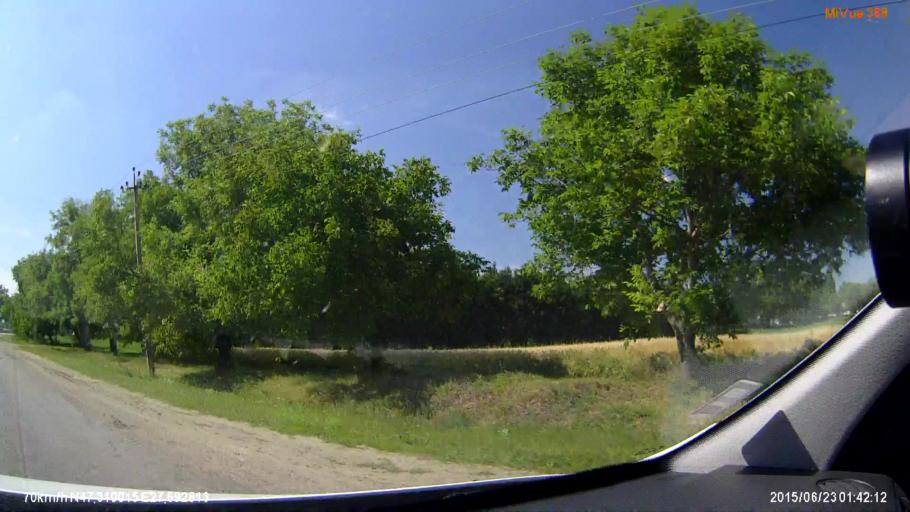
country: RO
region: Iasi
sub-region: Comuna Golaesti
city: Golaesti
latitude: 47.3100
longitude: 27.6931
